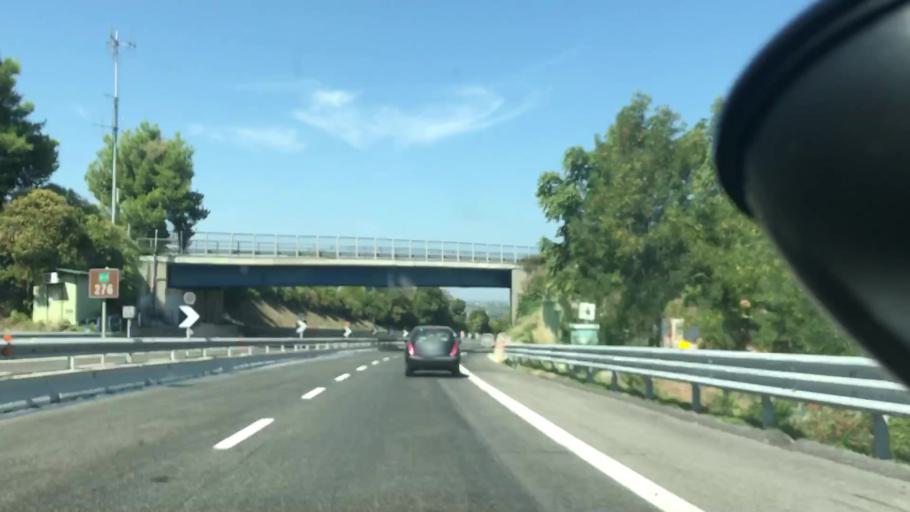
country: IT
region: Abruzzo
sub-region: Provincia di Chieti
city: Vasto
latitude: 42.1363
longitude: 14.6628
